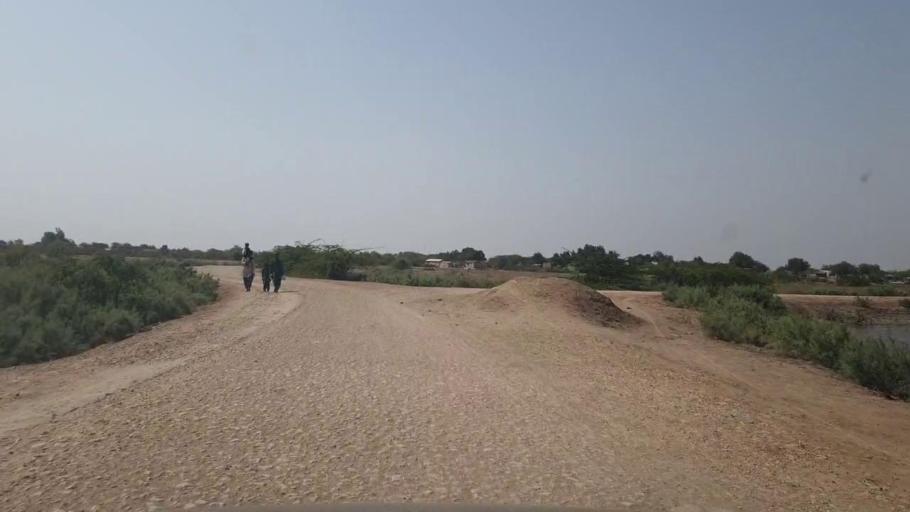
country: PK
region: Sindh
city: Jati
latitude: 24.3585
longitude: 68.5552
